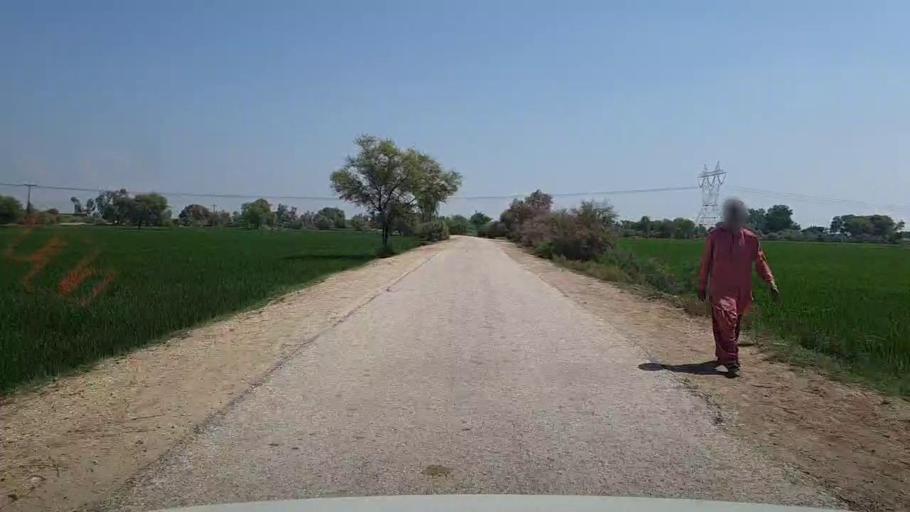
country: PK
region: Sindh
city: Kandhkot
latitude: 28.3069
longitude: 69.3427
